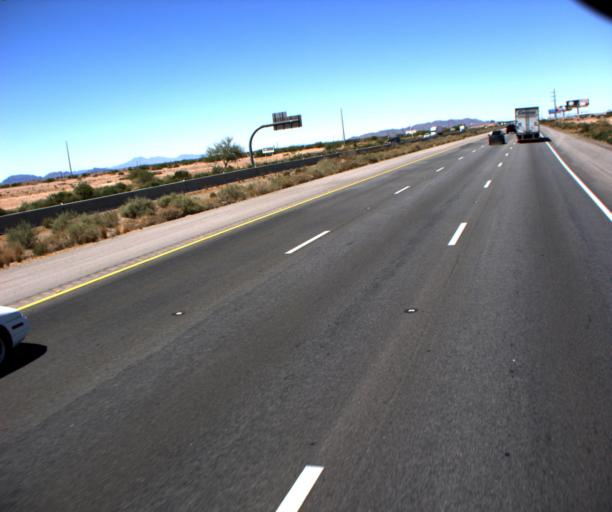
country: US
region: Arizona
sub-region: Pinal County
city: Eloy
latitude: 32.7404
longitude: -111.5599
